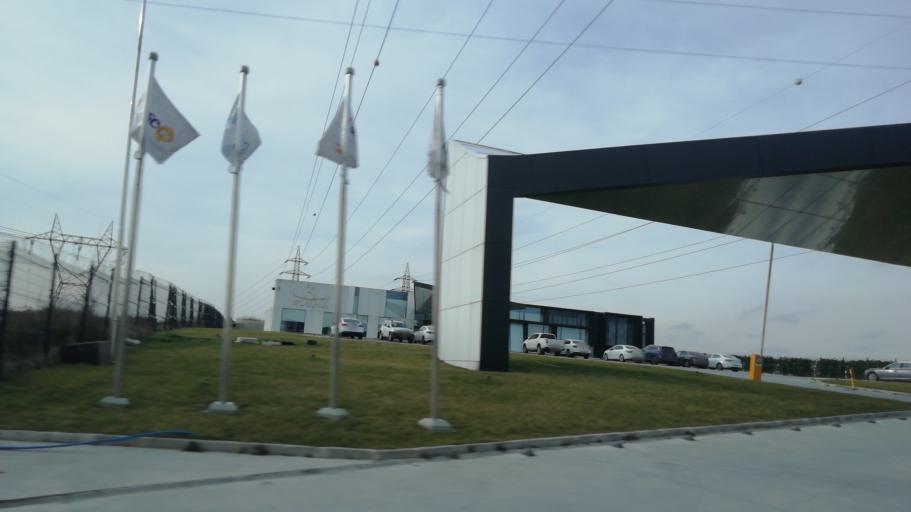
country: TR
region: Istanbul
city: Basaksehir
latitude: 41.1172
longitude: 28.7990
